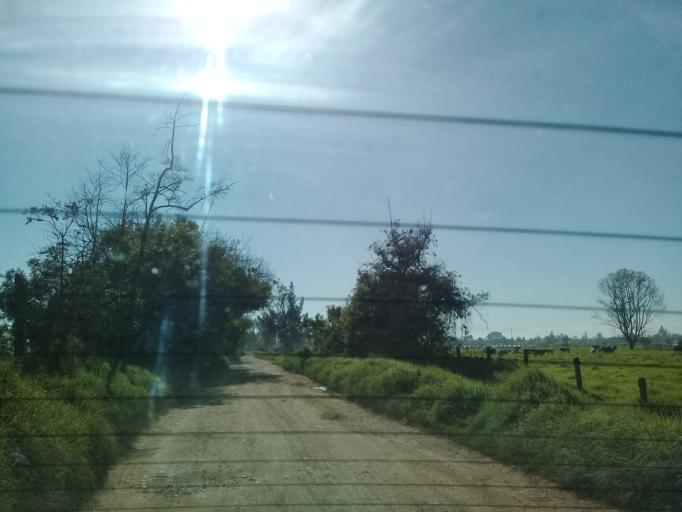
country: CO
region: Cundinamarca
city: Madrid
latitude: 4.7518
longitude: -74.2391
